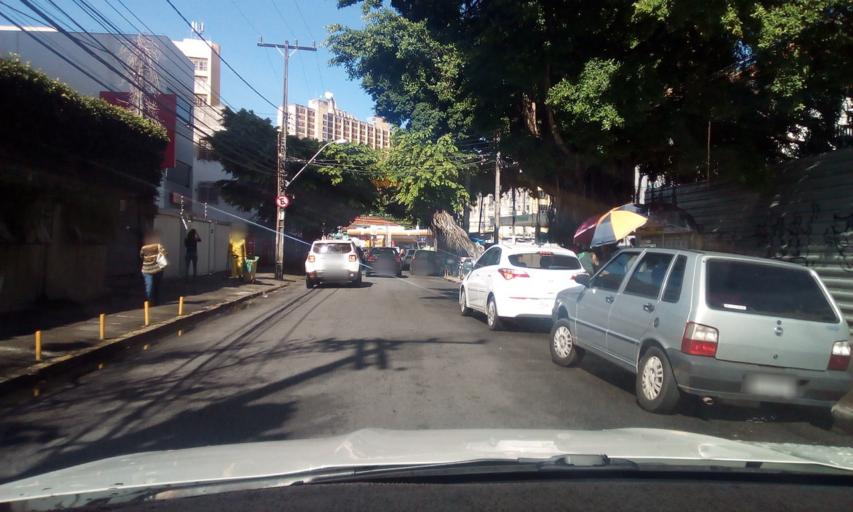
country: BR
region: Pernambuco
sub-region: Recife
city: Recife
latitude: -8.0557
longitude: -34.8921
